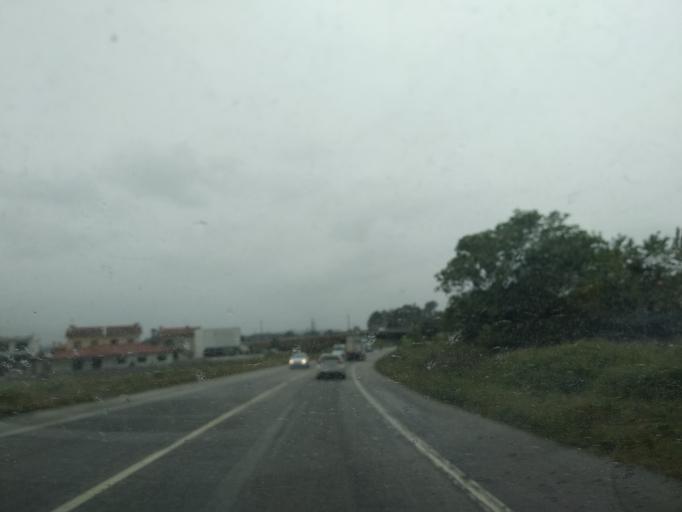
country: PT
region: Braga
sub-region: Barcelos
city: Barcelos
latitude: 41.5148
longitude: -8.6215
